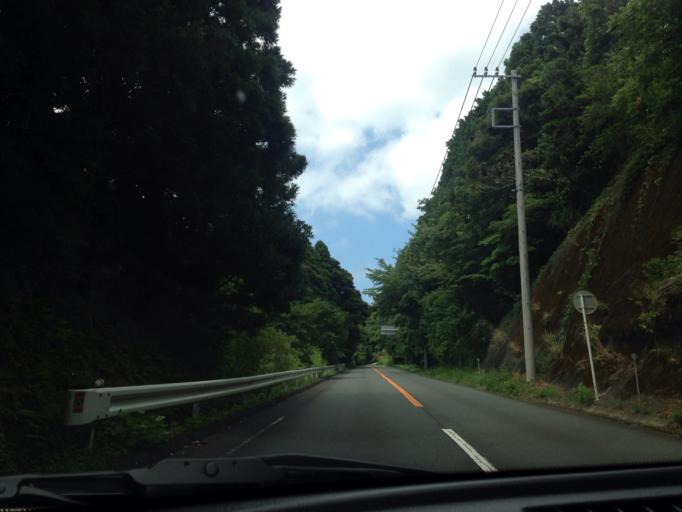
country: JP
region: Shizuoka
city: Shimoda
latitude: 34.7049
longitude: 138.7587
